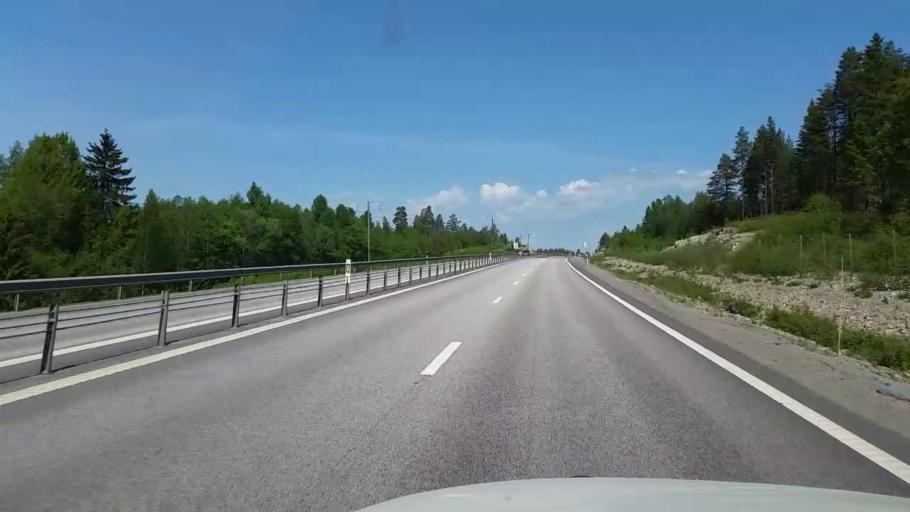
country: SE
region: Gaevleborg
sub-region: Hudiksvalls Kommun
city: Hudiksvall
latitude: 61.7291
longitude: 17.0653
